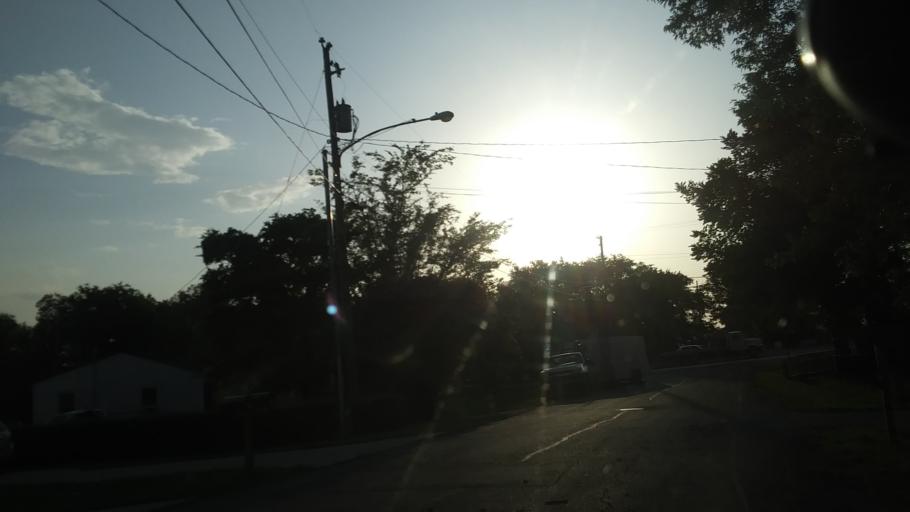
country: US
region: Tennessee
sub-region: Davidson County
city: Belle Meade
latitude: 36.1587
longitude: -86.8758
